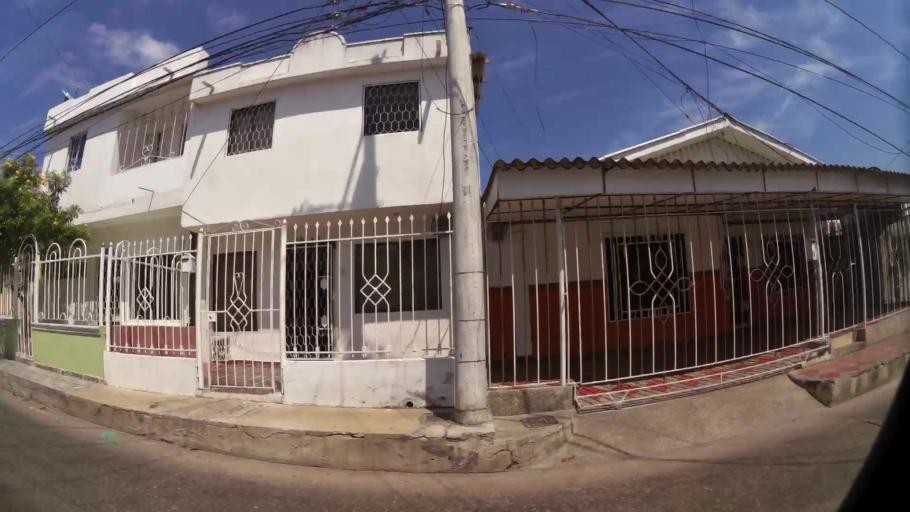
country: CO
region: Atlantico
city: Barranquilla
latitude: 10.9624
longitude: -74.8015
